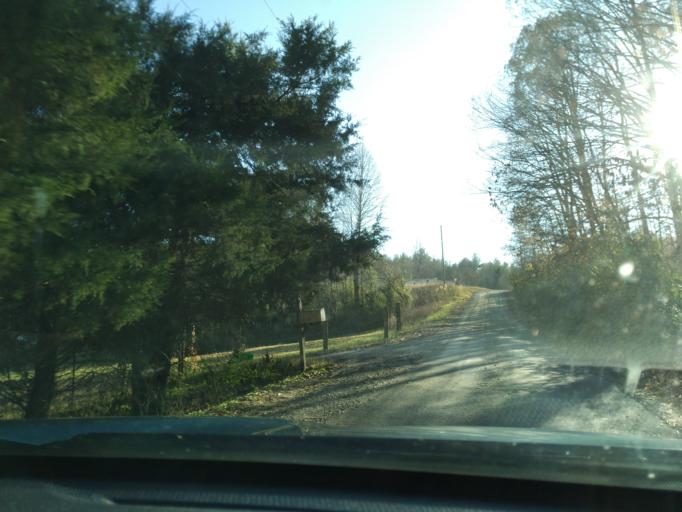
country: US
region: Virginia
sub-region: Floyd County
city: Floyd
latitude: 36.8390
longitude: -80.1910
